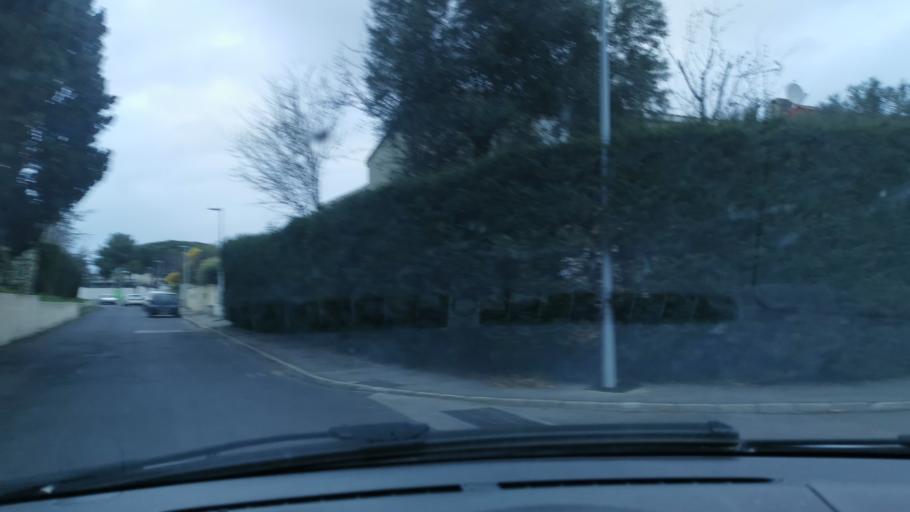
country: FR
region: Languedoc-Roussillon
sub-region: Departement de l'Herault
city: Villeneuve-les-Maguelone
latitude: 43.5582
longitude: 3.8751
